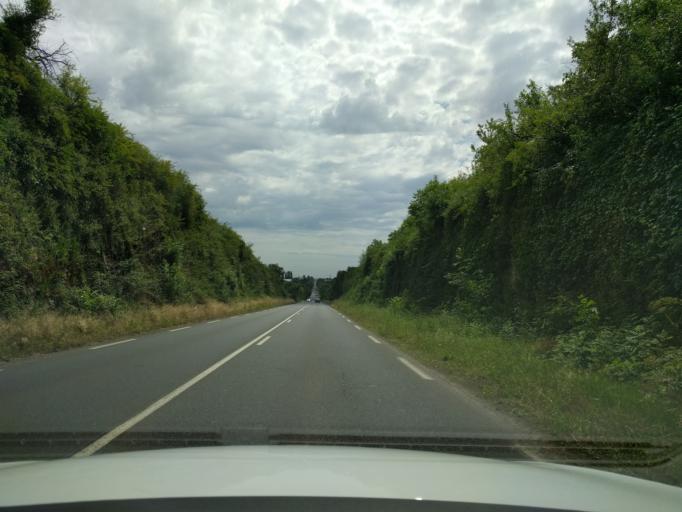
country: FR
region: Poitou-Charentes
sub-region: Departement des Deux-Sevres
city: Bessines
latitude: 46.3457
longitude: -0.5030
